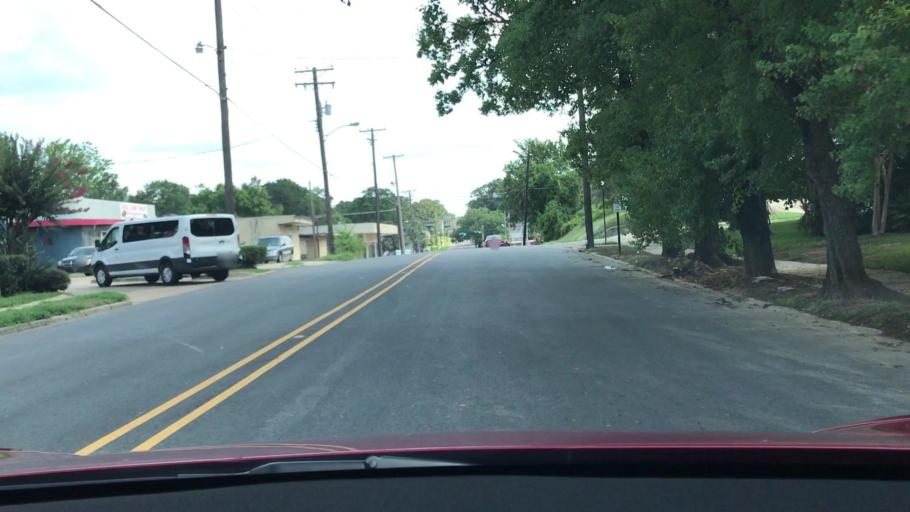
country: US
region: Louisiana
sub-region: Bossier Parish
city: Bossier City
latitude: 32.4939
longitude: -93.7333
